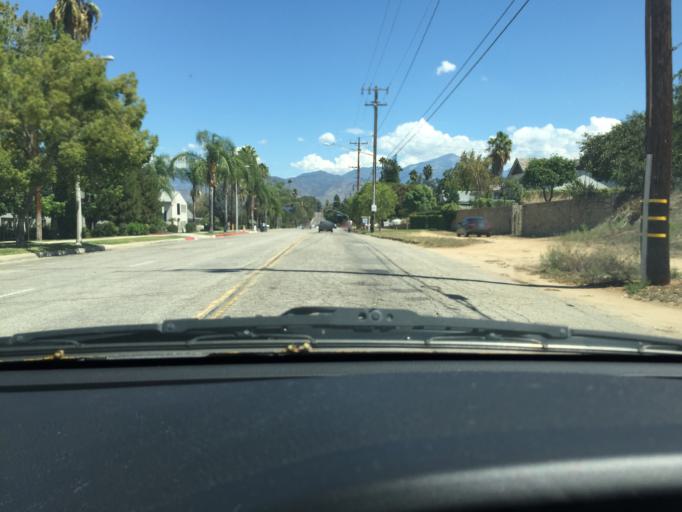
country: US
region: California
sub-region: San Bernardino County
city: Redlands
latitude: 34.0436
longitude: -117.1677
